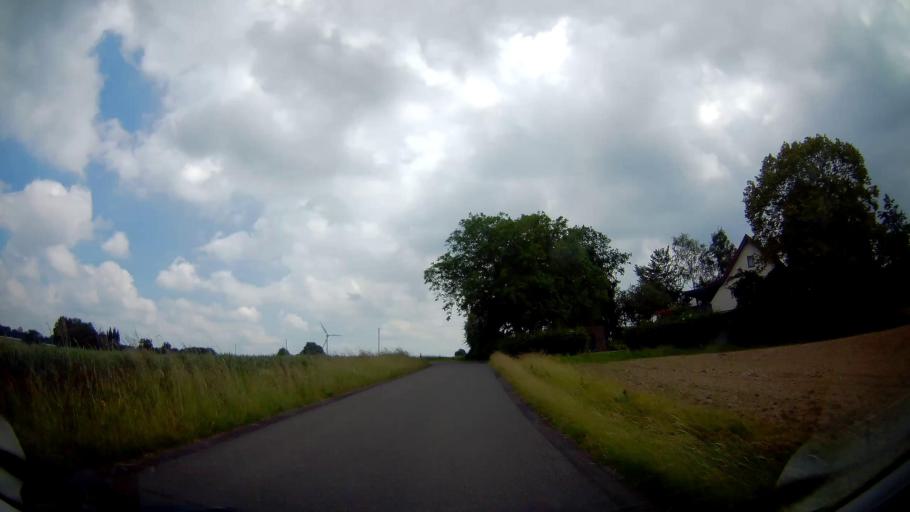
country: DE
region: North Rhine-Westphalia
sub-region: Regierungsbezirk Detmold
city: Herford
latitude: 52.1291
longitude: 8.7194
